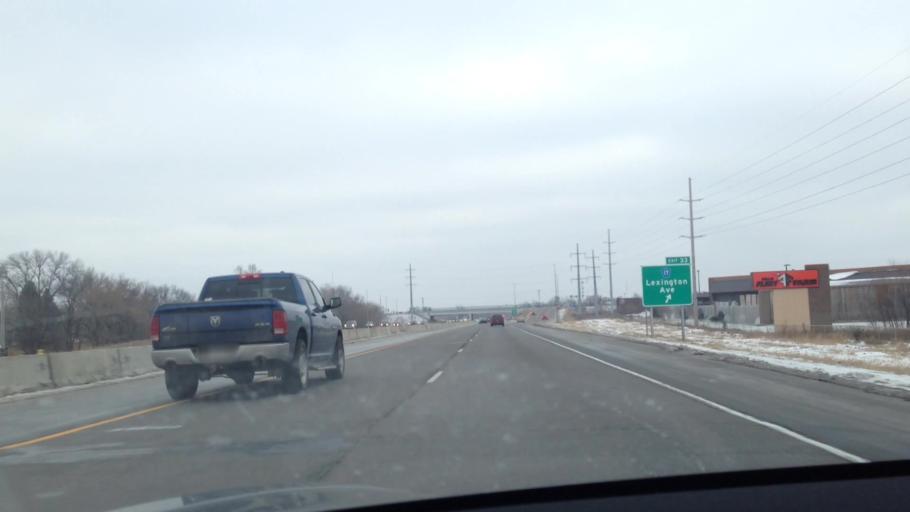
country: US
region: Minnesota
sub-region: Anoka County
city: Lexington
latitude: 45.1551
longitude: -93.1690
